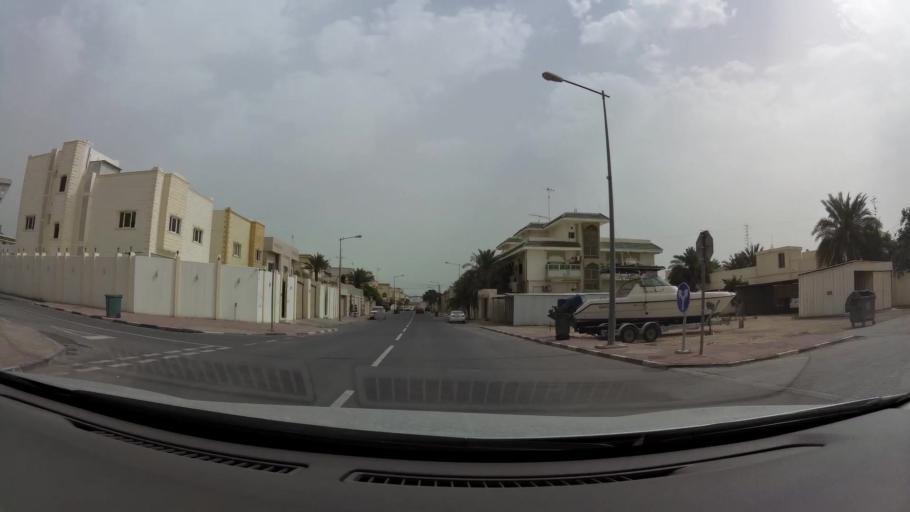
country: QA
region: Baladiyat ad Dawhah
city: Doha
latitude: 25.2600
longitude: 51.5435
